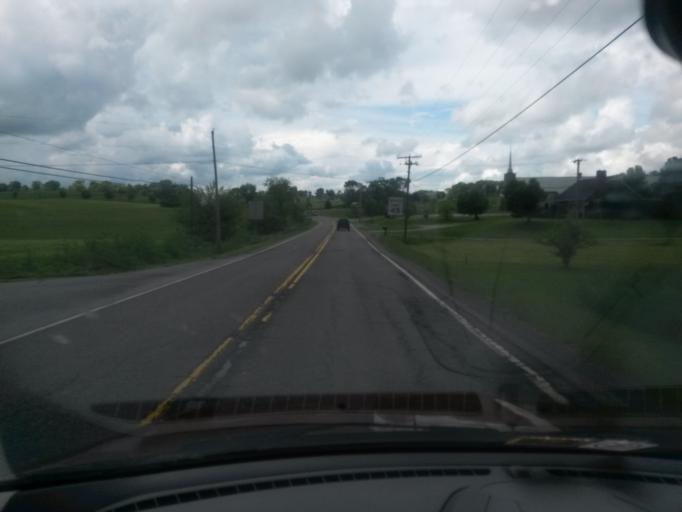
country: US
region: Virginia
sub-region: Montgomery County
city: Christiansburg
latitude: 37.0693
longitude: -80.4423
